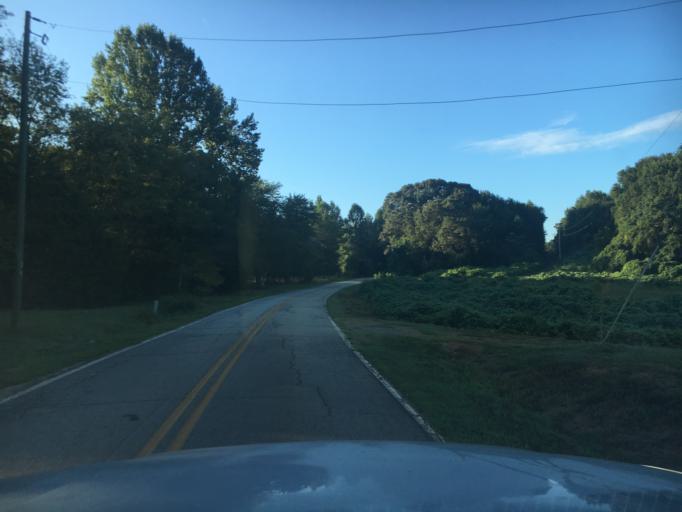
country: US
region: South Carolina
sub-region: Spartanburg County
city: Woodruff
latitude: 34.7606
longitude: -81.9611
